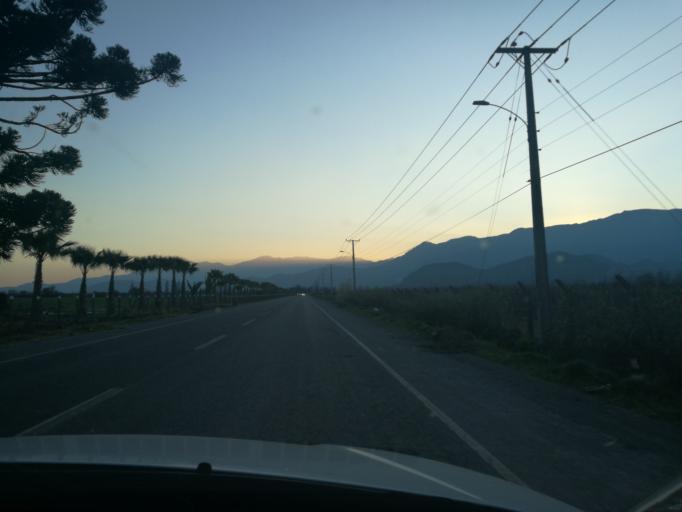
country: CL
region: O'Higgins
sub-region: Provincia de Cachapoal
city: Graneros
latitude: -34.0358
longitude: -70.6796
